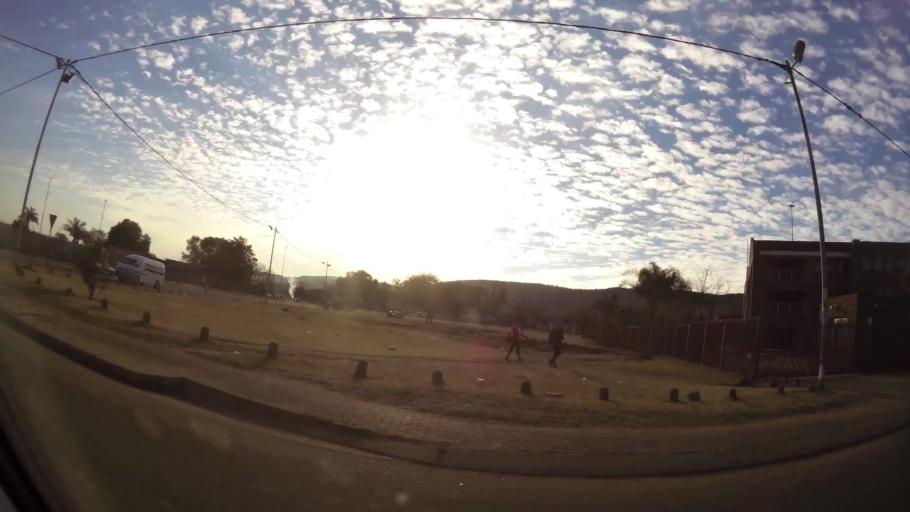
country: ZA
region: Gauteng
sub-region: City of Tshwane Metropolitan Municipality
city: Cullinan
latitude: -25.7097
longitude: 28.3777
